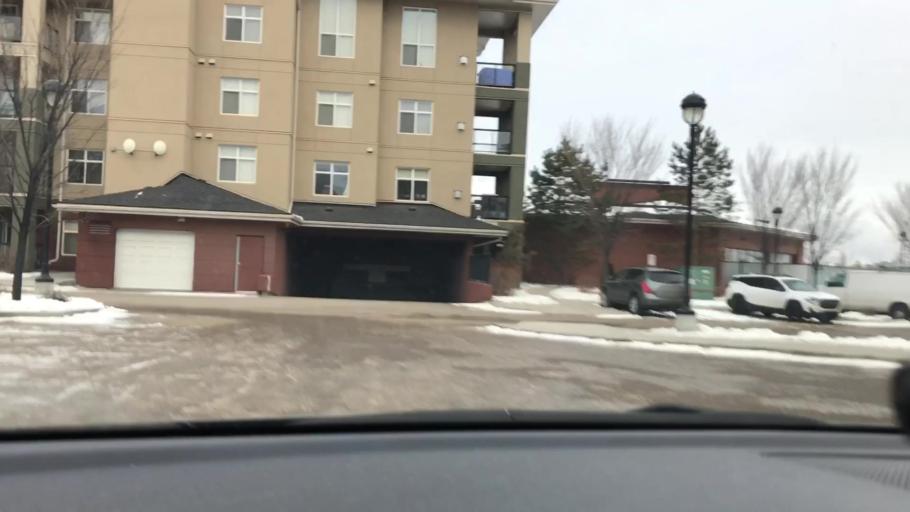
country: CA
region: Alberta
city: Edmonton
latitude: 53.5149
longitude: -113.4357
